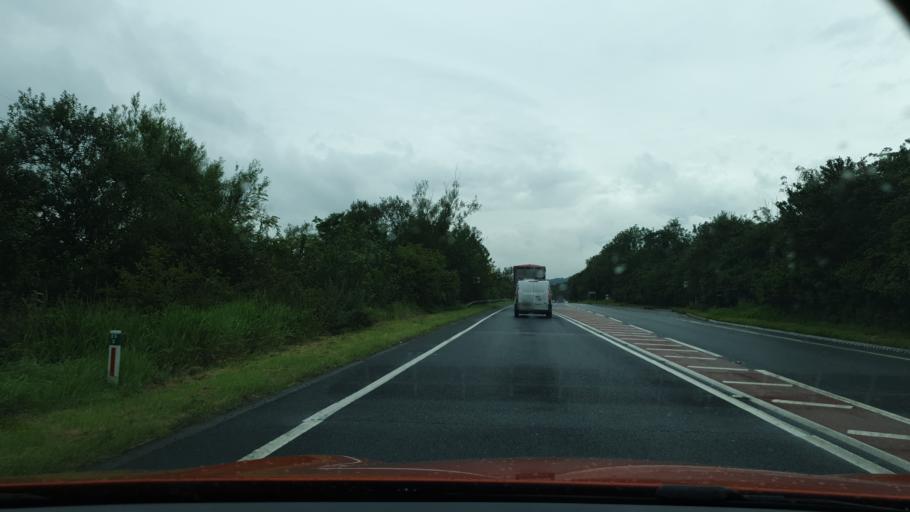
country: GB
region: England
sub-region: Cumbria
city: Arnside
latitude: 54.2487
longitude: -2.8396
